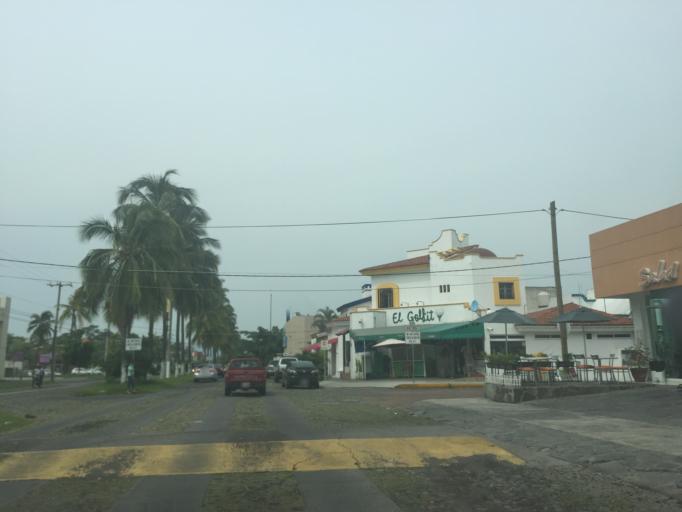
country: MX
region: Colima
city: Colima
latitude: 19.2575
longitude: -103.7159
